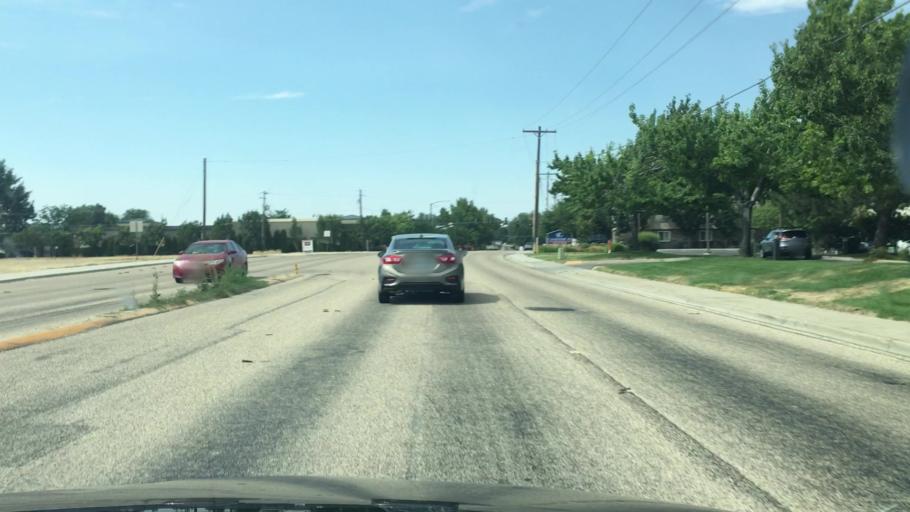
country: US
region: Idaho
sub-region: Ada County
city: Garden City
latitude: 43.6104
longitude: -116.2740
